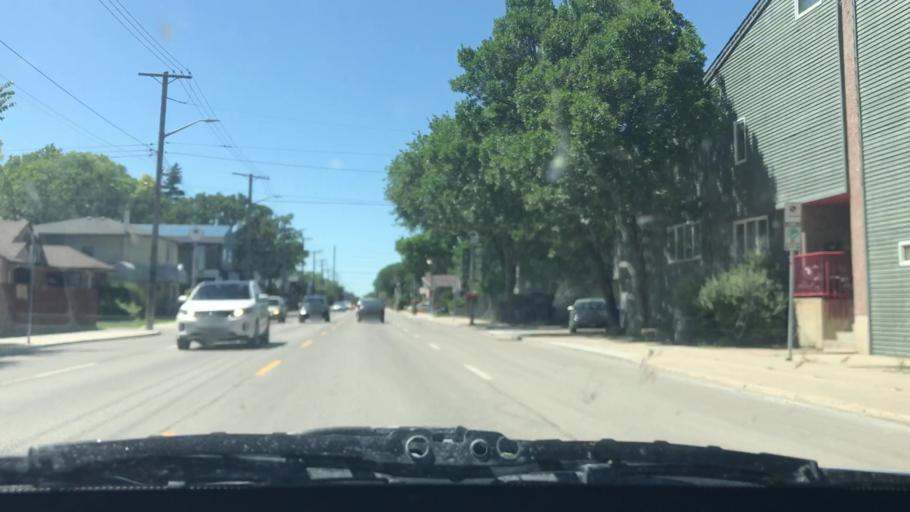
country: CA
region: Manitoba
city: Winnipeg
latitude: 49.8741
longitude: -97.1904
